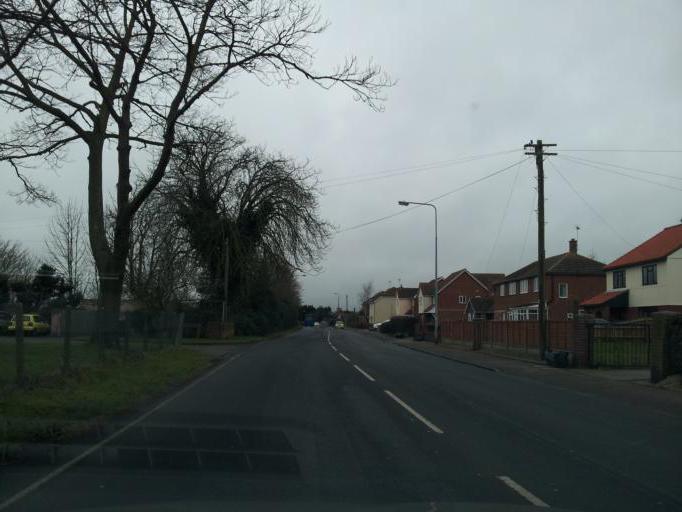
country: GB
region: England
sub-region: Essex
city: Dovercourt
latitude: 51.9276
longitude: 1.2412
